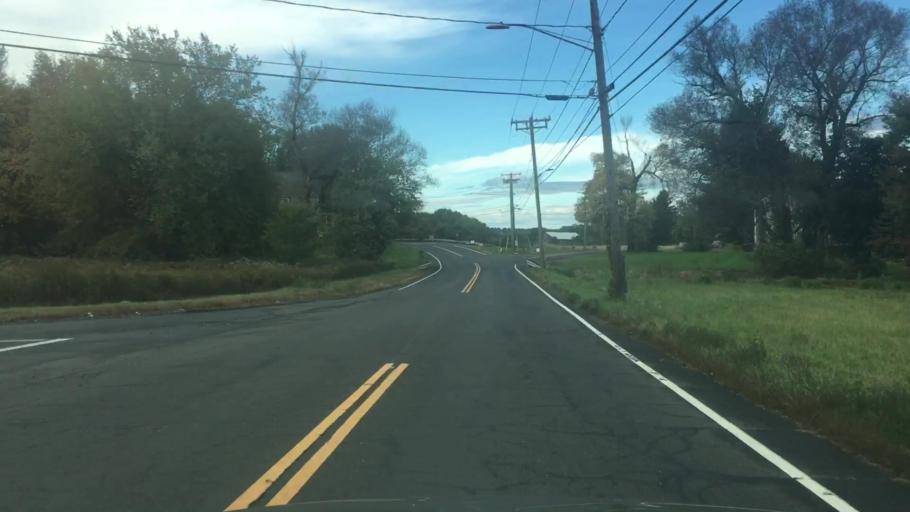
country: US
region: Connecticut
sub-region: Hartford County
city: Hazardville
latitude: 41.9598
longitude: -72.5262
